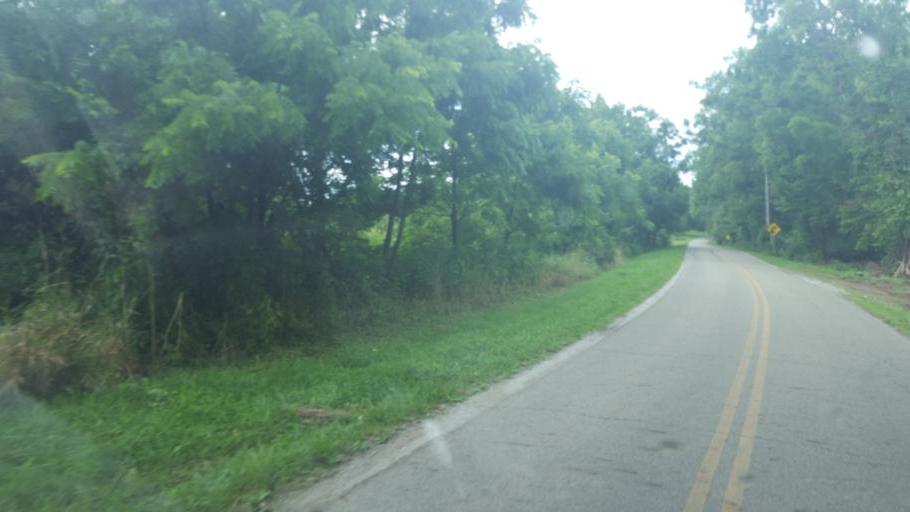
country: US
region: Ohio
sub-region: Pickaway County
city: Ashville
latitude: 39.7065
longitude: -82.9377
